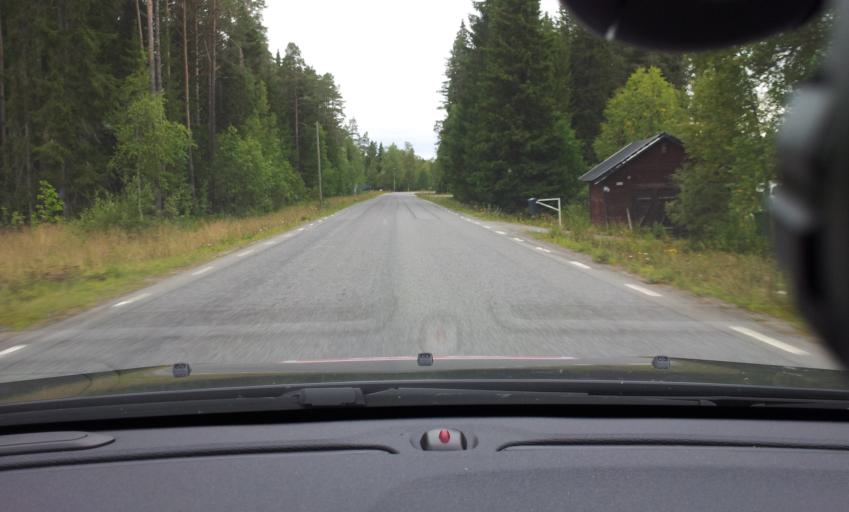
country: SE
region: Jaemtland
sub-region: OEstersunds Kommun
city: Brunflo
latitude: 63.0472
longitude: 14.8635
